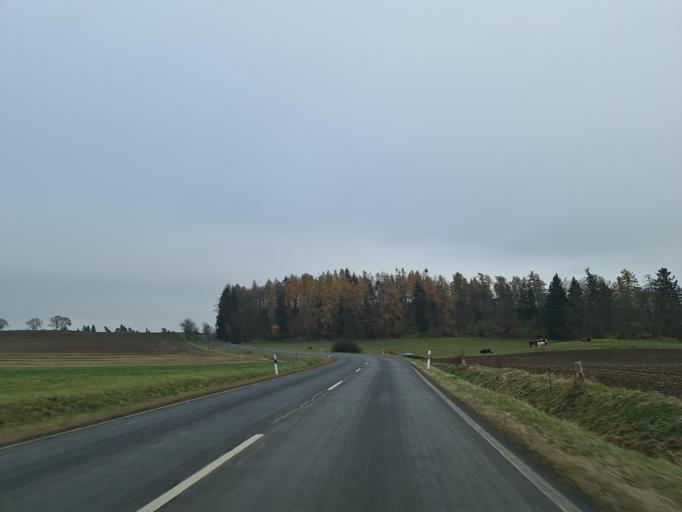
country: DE
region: Saxony
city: Syrau
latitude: 50.5072
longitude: 12.0599
